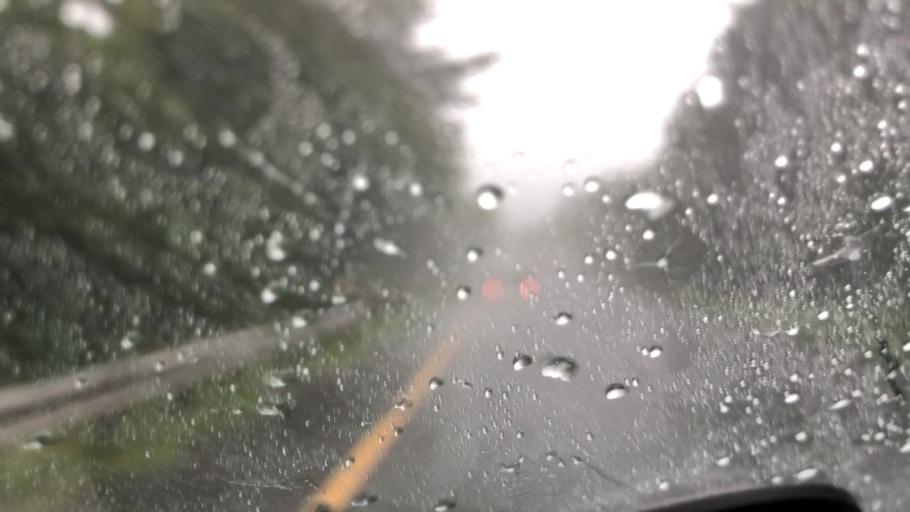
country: US
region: Massachusetts
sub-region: Hampden County
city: Westfield
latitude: 42.1562
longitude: -72.7941
